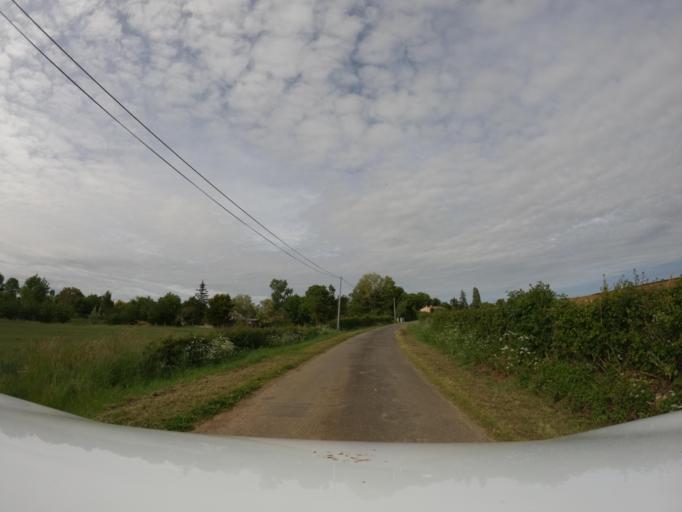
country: FR
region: Pays de la Loire
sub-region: Departement de la Vendee
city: Saint-Hilaire-des-Loges
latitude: 46.4885
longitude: -0.6620
